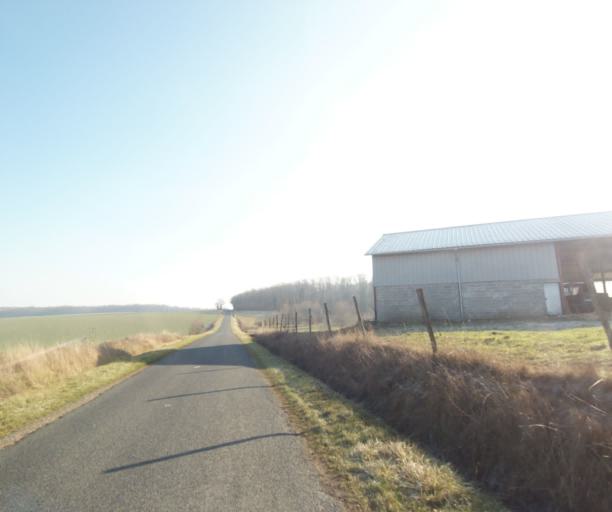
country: FR
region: Champagne-Ardenne
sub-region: Departement de la Haute-Marne
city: Chevillon
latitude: 48.4918
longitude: 5.0738
